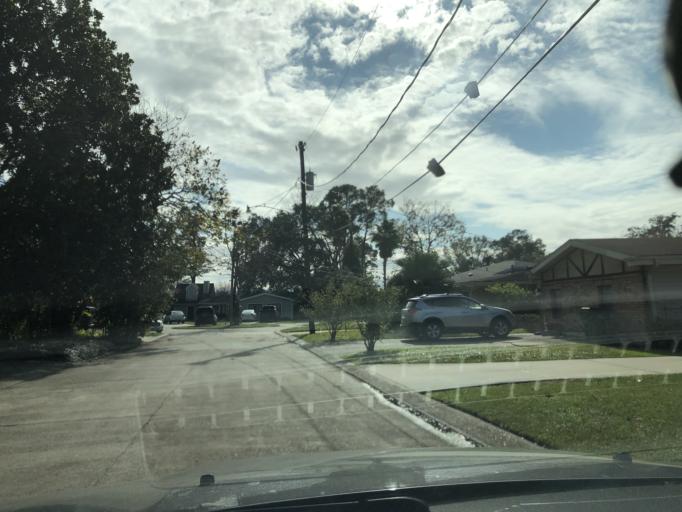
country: US
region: Louisiana
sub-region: Jefferson Parish
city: Metairie Terrace
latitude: 29.9852
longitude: -90.1661
